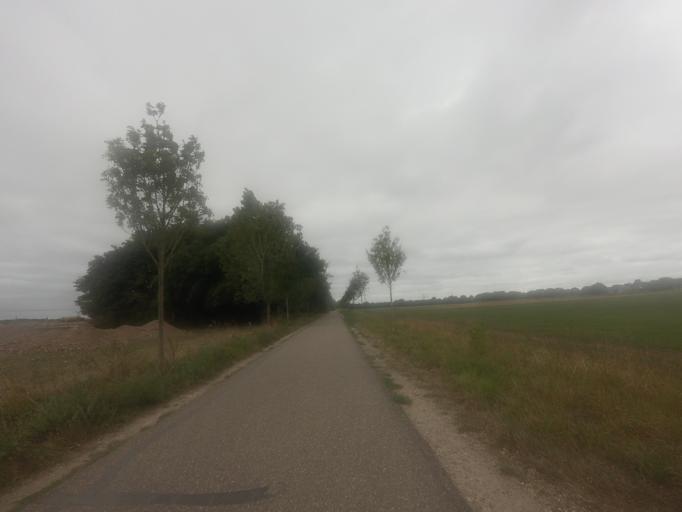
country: NL
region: North Brabant
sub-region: Gemeente Grave
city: Grave
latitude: 51.7877
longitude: 5.7559
